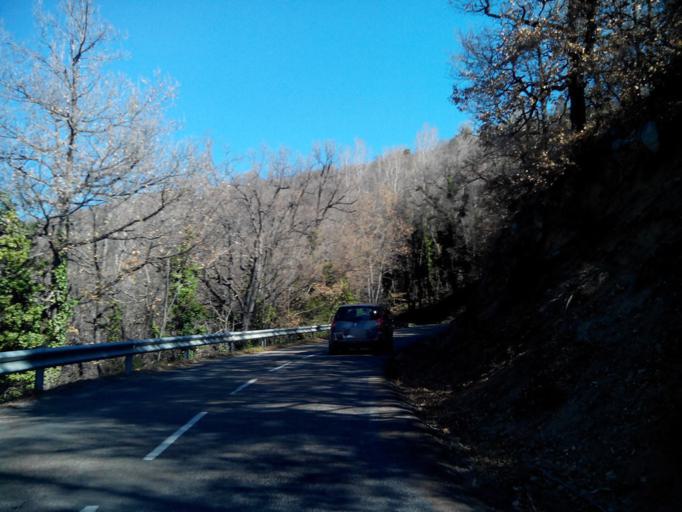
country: ES
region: Catalonia
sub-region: Provincia de Lleida
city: Lles de Cerdanya
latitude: 42.3761
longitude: 1.6796
